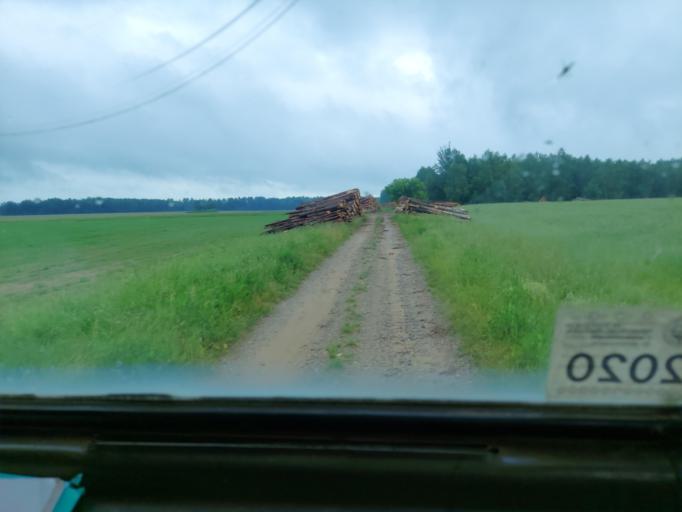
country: BY
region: Mogilev
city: Poselok Voskhod
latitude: 53.6742
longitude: 30.3998
